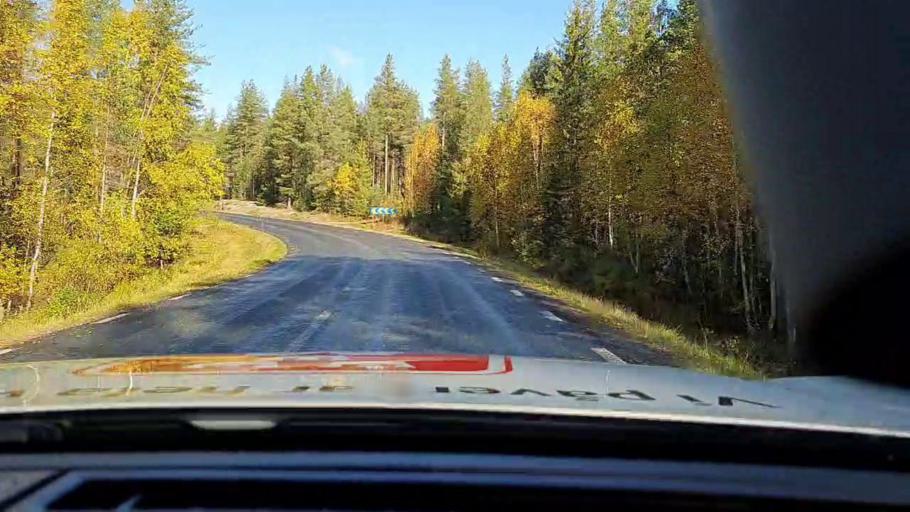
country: SE
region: Vaesterbotten
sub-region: Skelleftea Kommun
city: Langsele
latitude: 65.0015
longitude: 20.0912
